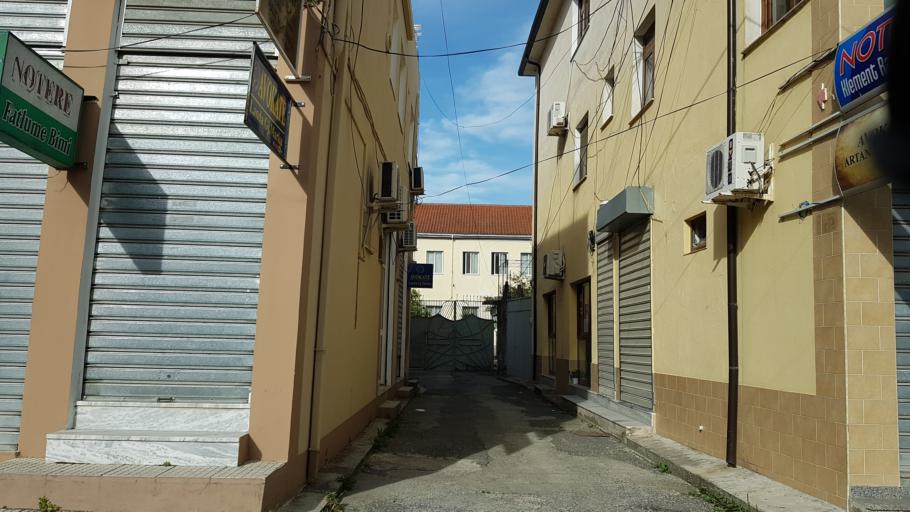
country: AL
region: Shkoder
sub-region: Rrethi i Shkodres
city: Shkoder
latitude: 42.0644
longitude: 19.5130
